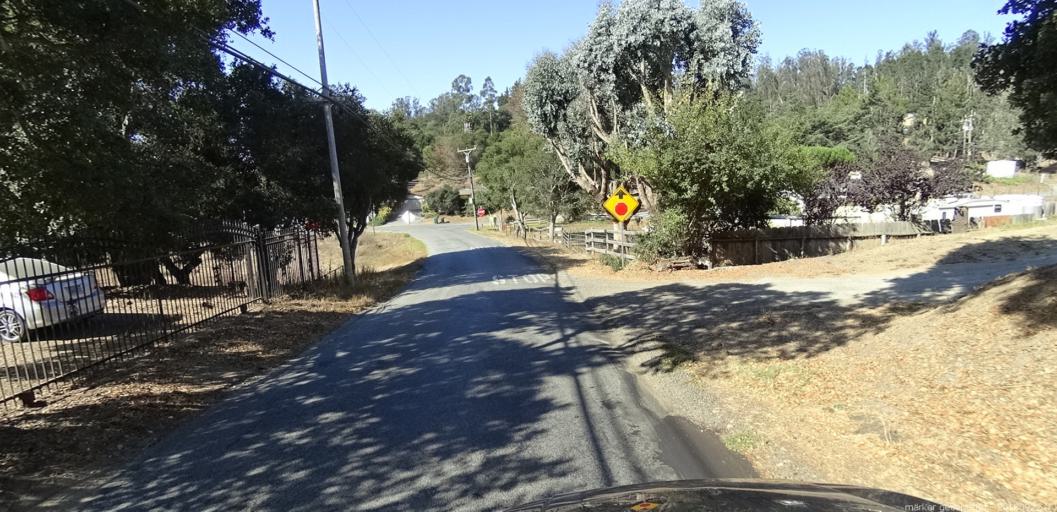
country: US
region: California
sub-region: Monterey County
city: Prunedale
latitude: 36.8087
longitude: -121.6485
